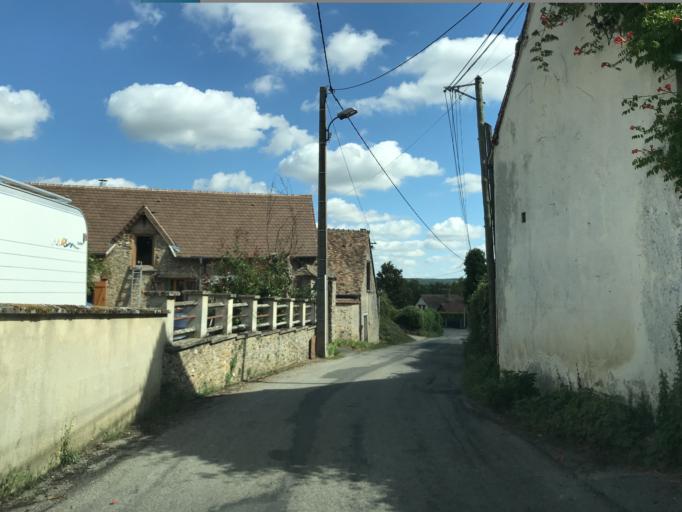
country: FR
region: Haute-Normandie
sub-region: Departement de l'Eure
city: La Chapelle-Reanville
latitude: 49.1393
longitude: 1.4034
